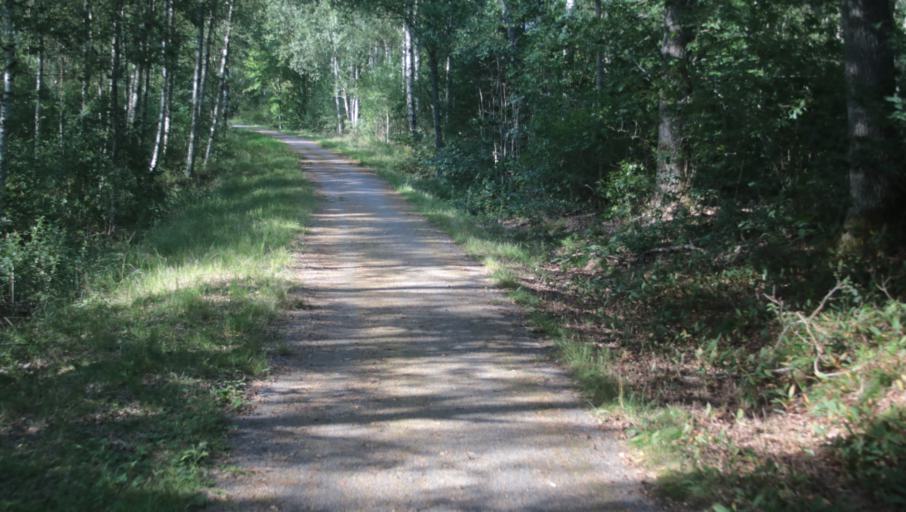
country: SE
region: Blekinge
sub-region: Karlshamns Kommun
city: Svangsta
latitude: 56.3232
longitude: 14.7052
